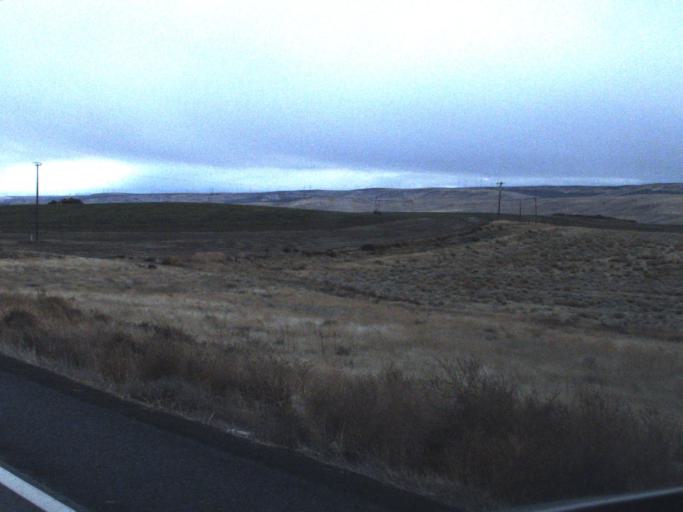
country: US
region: Washington
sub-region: Walla Walla County
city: Burbank
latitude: 46.0654
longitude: -118.7534
